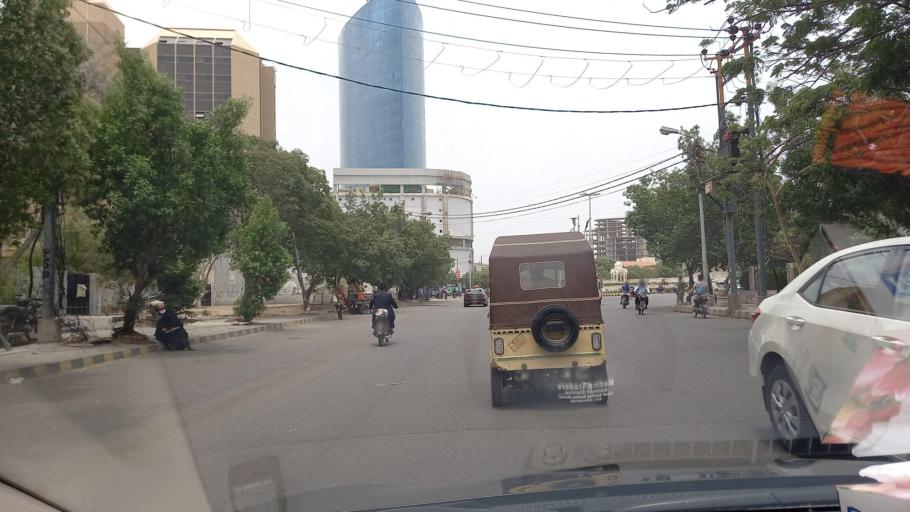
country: PK
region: Sindh
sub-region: Karachi District
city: Karachi
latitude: 24.8540
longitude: 67.0268
